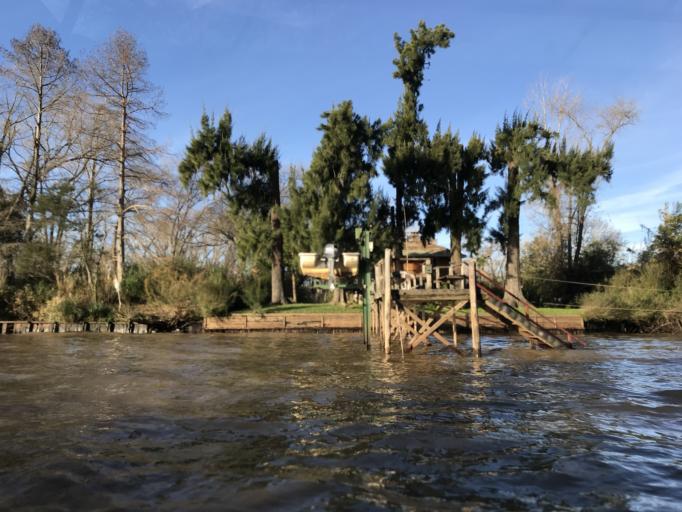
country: AR
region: Buenos Aires
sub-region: Partido de Tigre
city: Tigre
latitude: -34.4031
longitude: -58.5940
